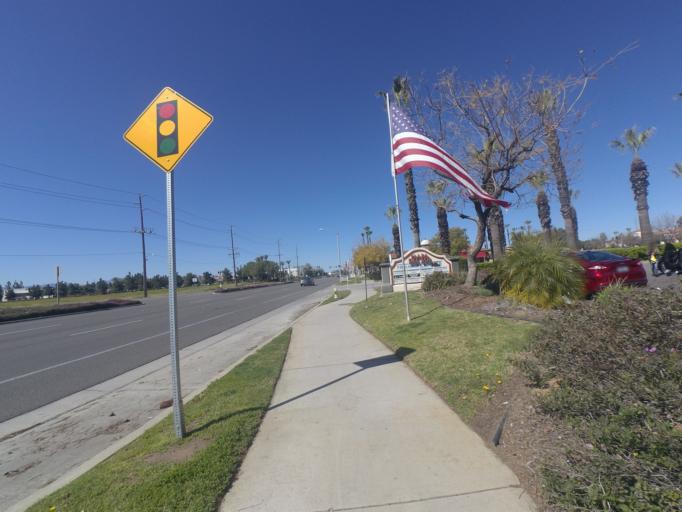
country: US
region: California
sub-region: Riverside County
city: March Air Force Base
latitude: 33.9174
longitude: -117.2590
